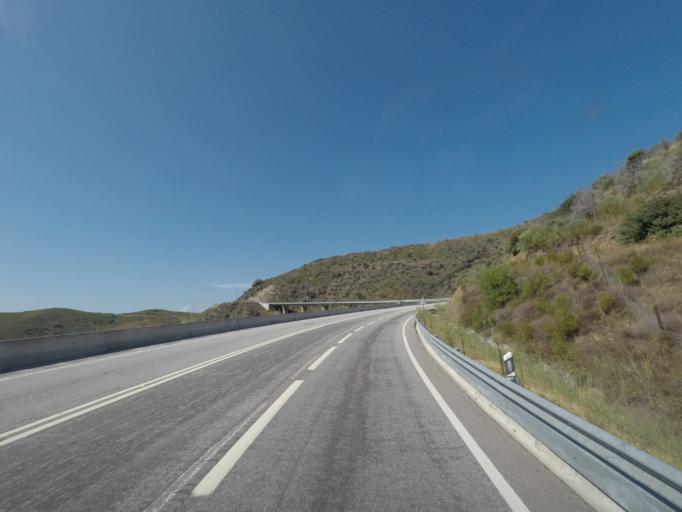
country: PT
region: Braganca
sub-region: Alfandega da Fe
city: Alfandega da Fe
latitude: 41.2793
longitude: -6.8842
